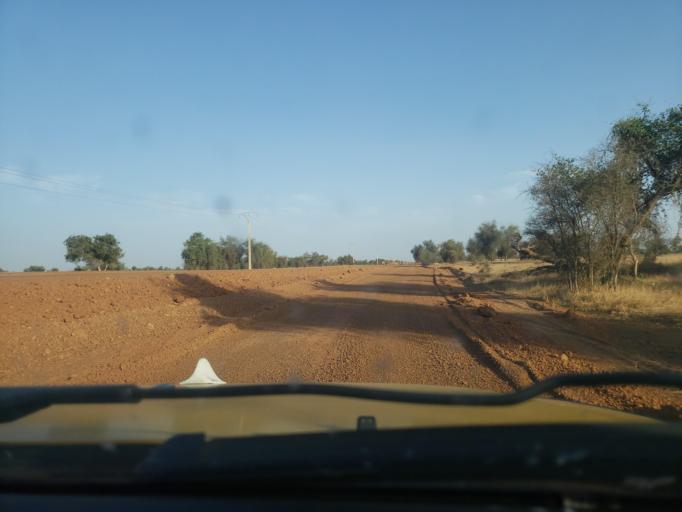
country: SN
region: Louga
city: Dara
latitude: 15.4263
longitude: -15.7397
